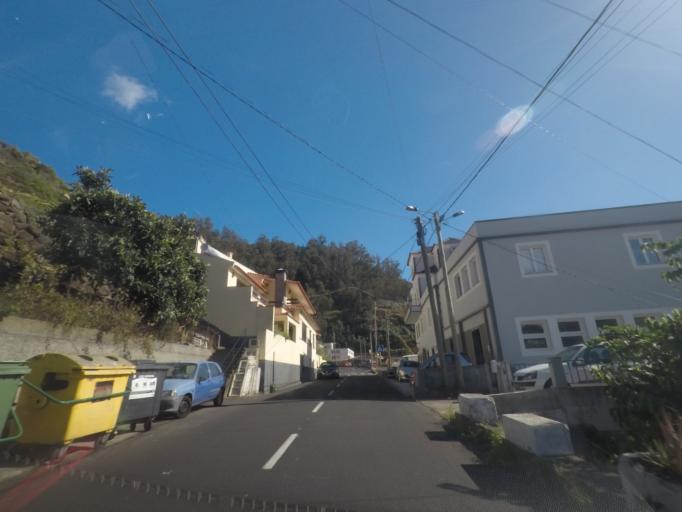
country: PT
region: Madeira
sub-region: Ribeira Brava
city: Campanario
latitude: 32.6707
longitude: -17.0213
